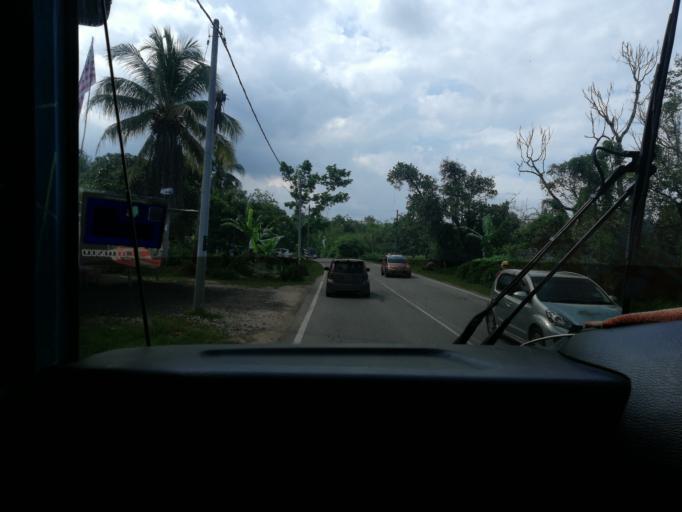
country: MY
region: Kedah
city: Kulim
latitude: 5.2974
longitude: 100.6233
